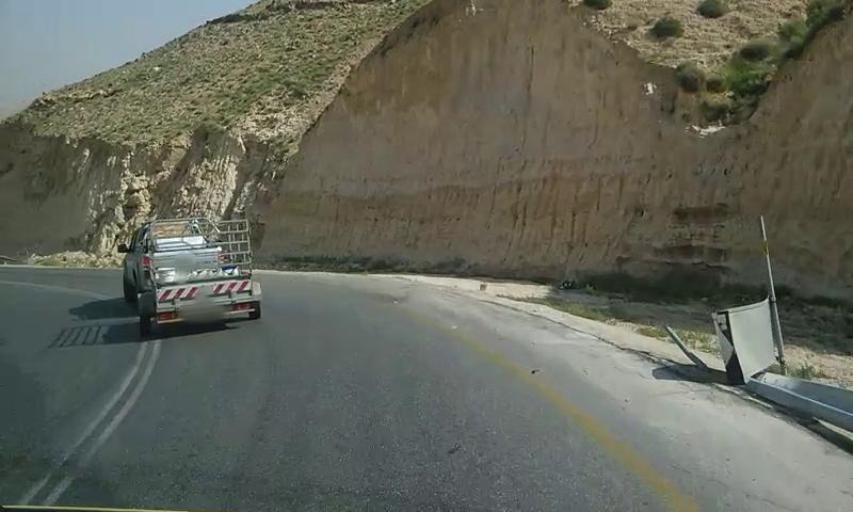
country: PS
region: West Bank
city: An Nuway`imah
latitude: 31.9122
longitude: 35.3833
